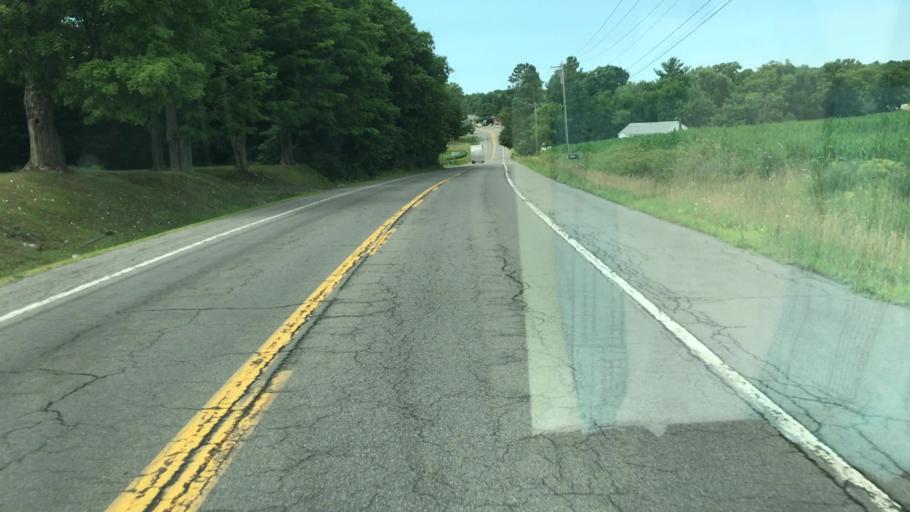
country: US
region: New York
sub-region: Onondaga County
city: Skaneateles
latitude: 42.9424
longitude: -76.3866
